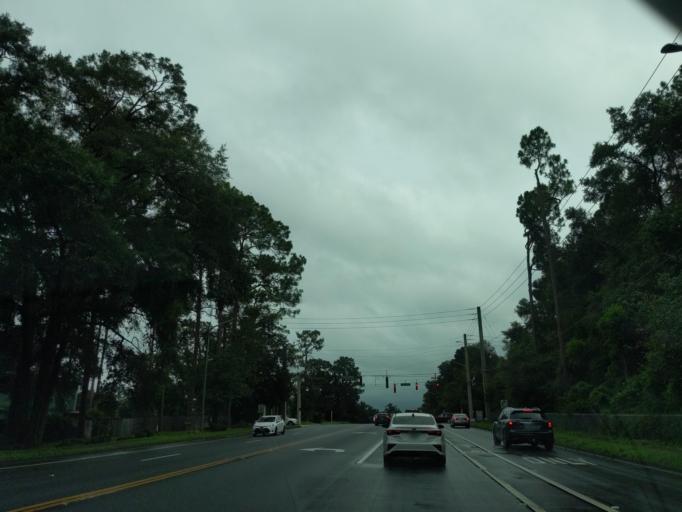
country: US
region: Florida
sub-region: Alachua County
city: Gainesville
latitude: 29.6460
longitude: -82.4225
